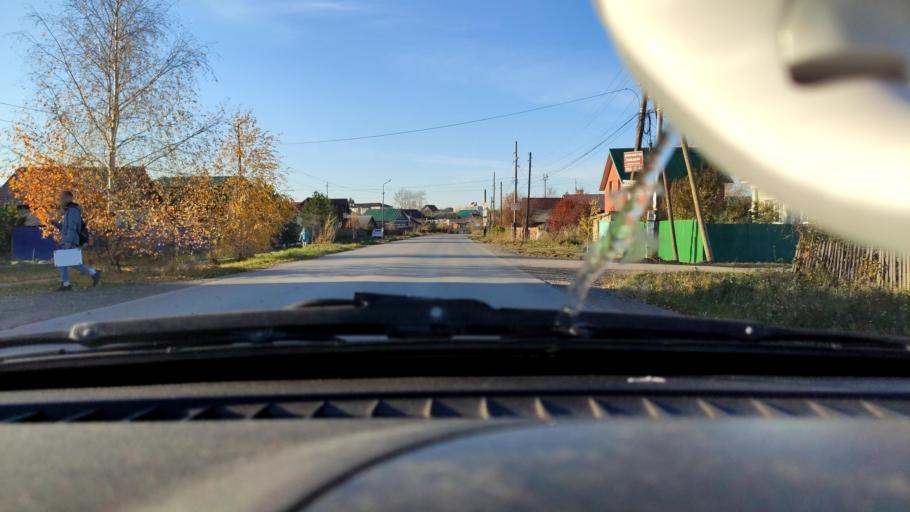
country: RU
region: Perm
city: Froly
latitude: 57.8837
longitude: 56.2594
